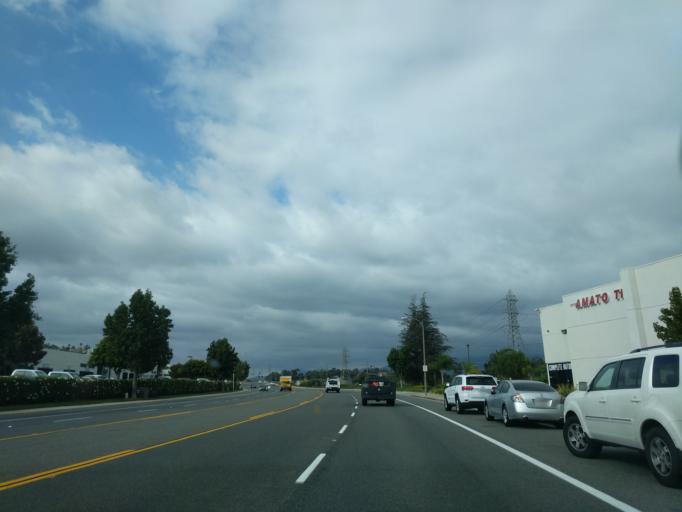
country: US
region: California
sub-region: Orange County
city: Mission Viejo
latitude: 33.5691
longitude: -117.6746
